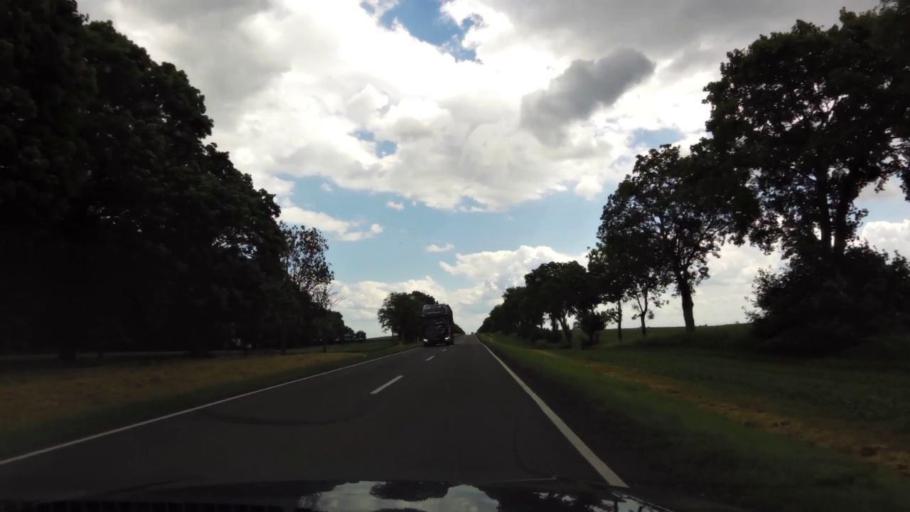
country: PL
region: West Pomeranian Voivodeship
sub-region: Powiat mysliborski
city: Mysliborz
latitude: 52.9641
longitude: 14.7519
